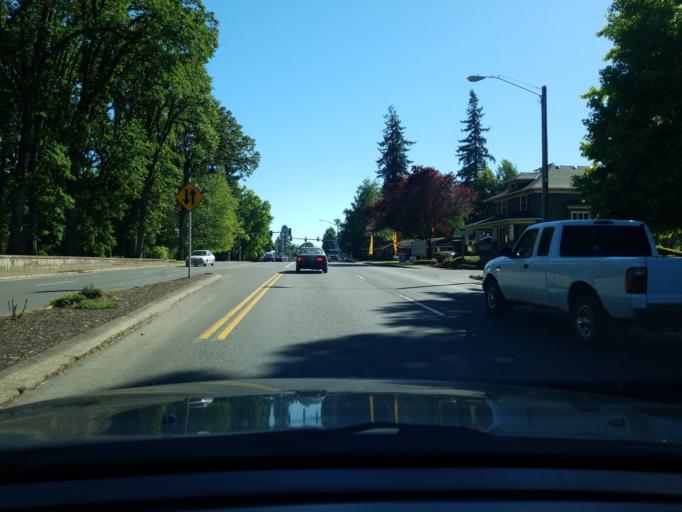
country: US
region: Oregon
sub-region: Yamhill County
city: McMinnville
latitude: 45.2032
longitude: -123.2009
